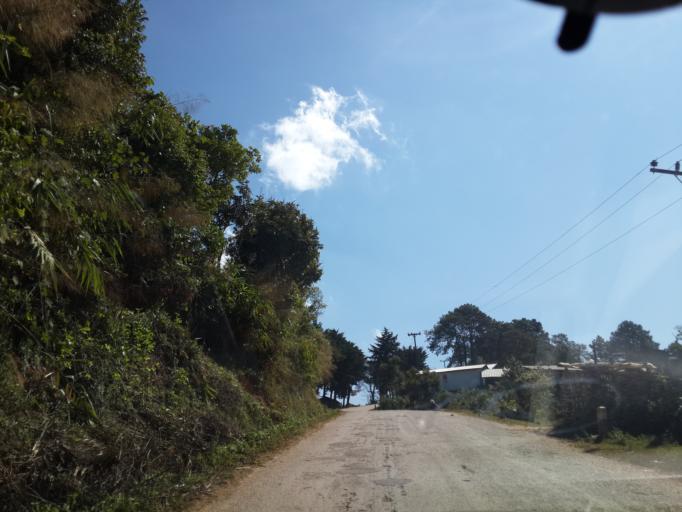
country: TH
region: Chiang Mai
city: Fang
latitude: 19.9351
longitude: 99.0422
